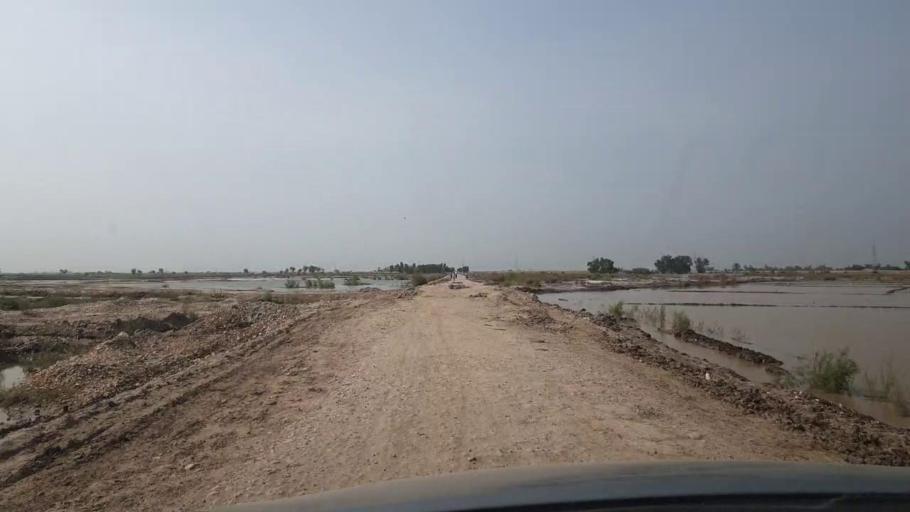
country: PK
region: Sindh
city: Lakhi
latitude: 27.8396
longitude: 68.6997
